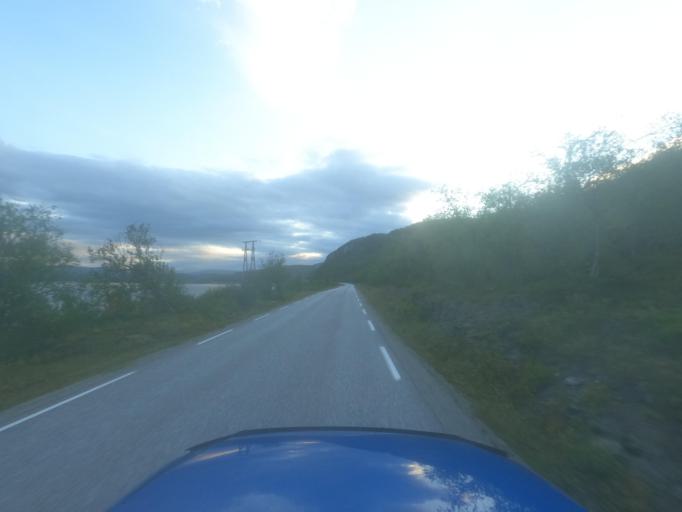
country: NO
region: Finnmark Fylke
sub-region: Porsanger
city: Lakselv
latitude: 70.2406
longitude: 24.9730
